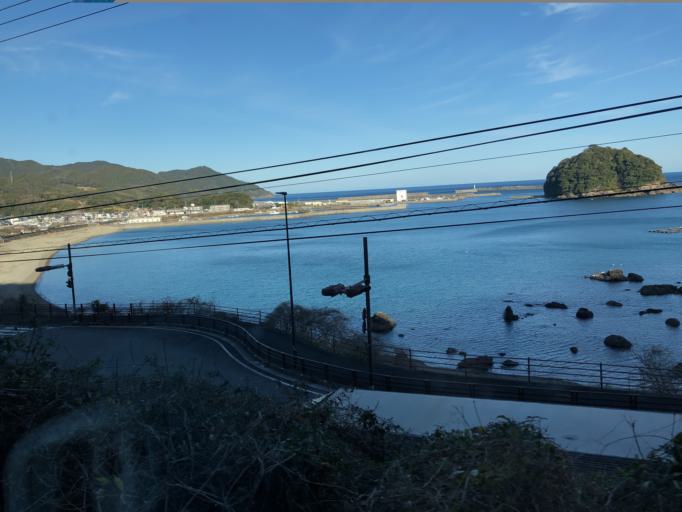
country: JP
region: Kochi
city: Nakamura
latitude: 33.0715
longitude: 133.1040
